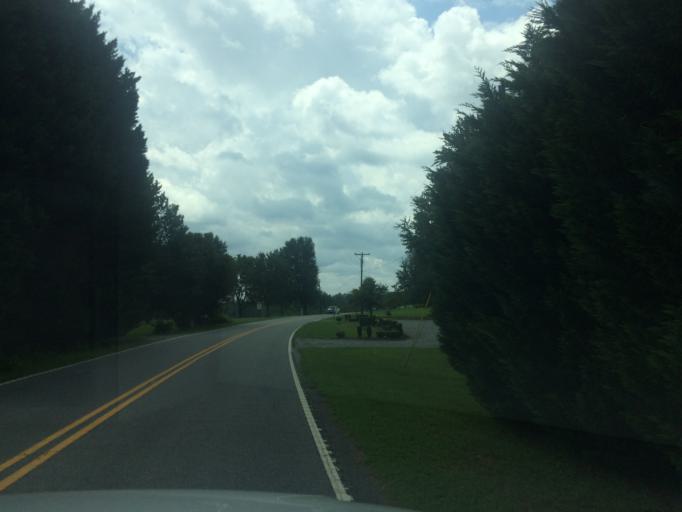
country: US
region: South Carolina
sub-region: Spartanburg County
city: Landrum
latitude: 35.2190
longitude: -82.0501
